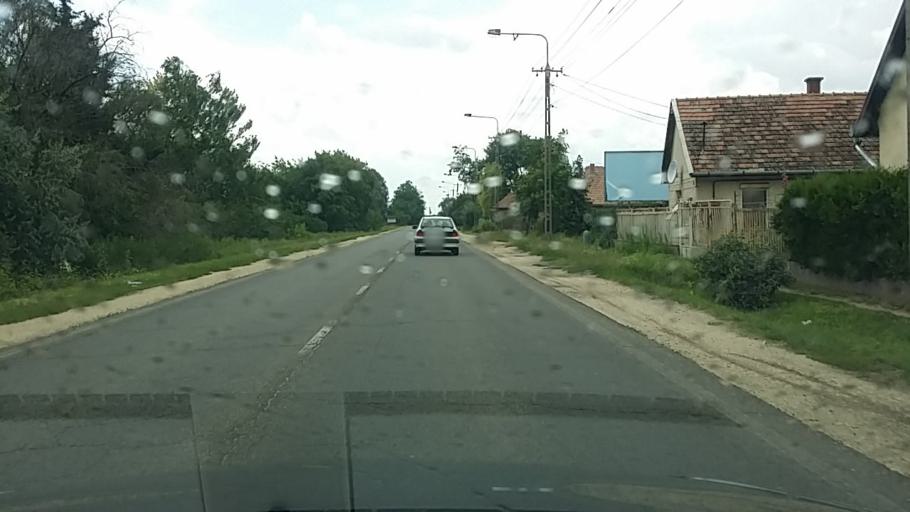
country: HU
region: Pest
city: Orkeny
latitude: 47.1329
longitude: 19.4166
